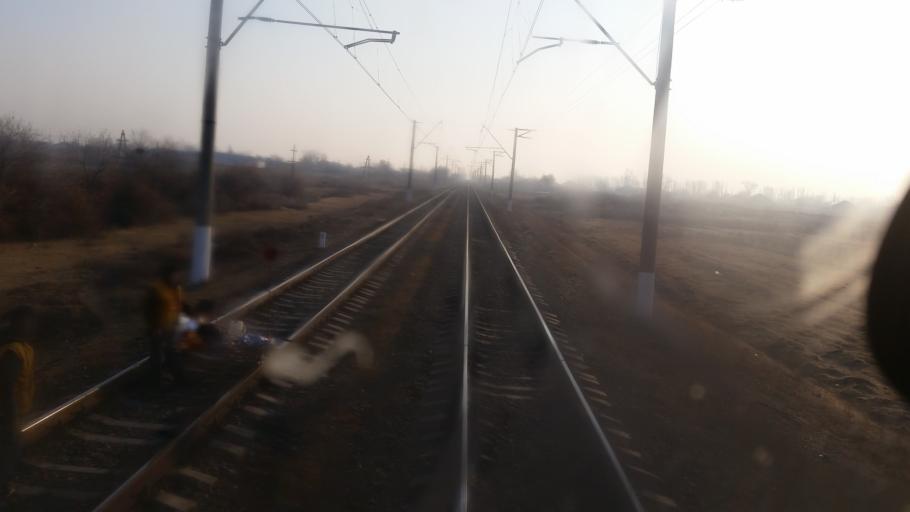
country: AZ
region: Yevlax
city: Aran
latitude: 40.6314
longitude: 47.0531
